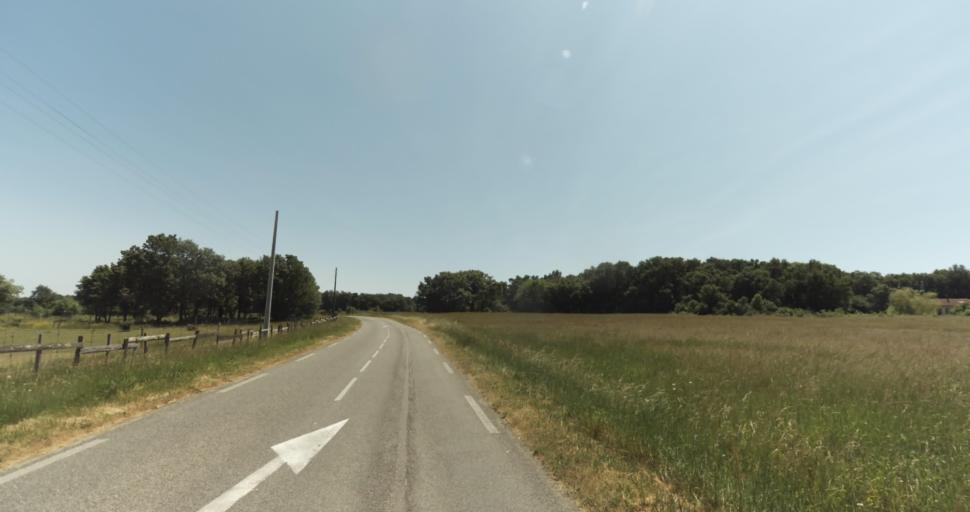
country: FR
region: Midi-Pyrenees
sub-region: Departement de la Haute-Garonne
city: Levignac
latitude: 43.6271
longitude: 1.1842
